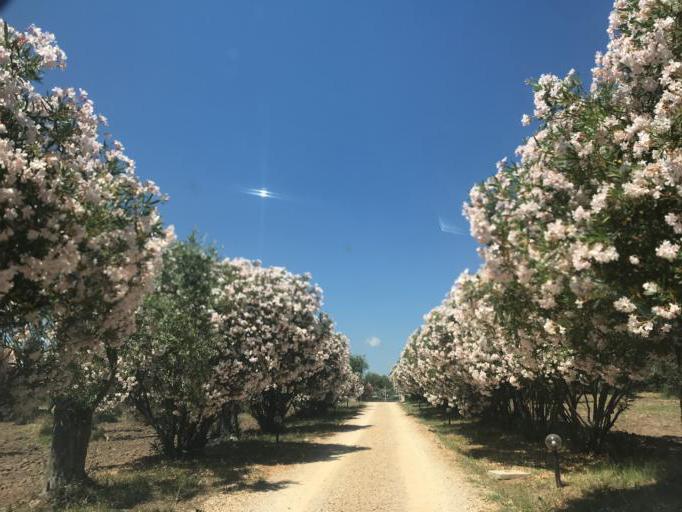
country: IT
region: Sardinia
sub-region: Provincia di Sassari
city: Alghero
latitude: 40.5493
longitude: 8.3464
